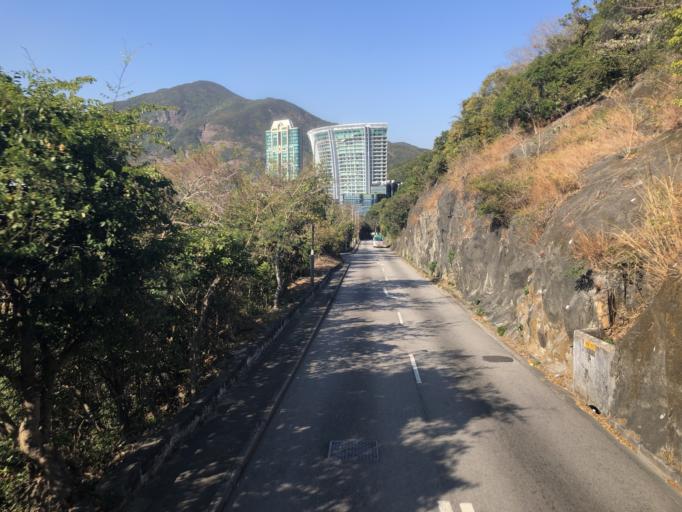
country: HK
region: Wanchai
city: Wan Chai
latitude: 22.2309
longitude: 114.1995
